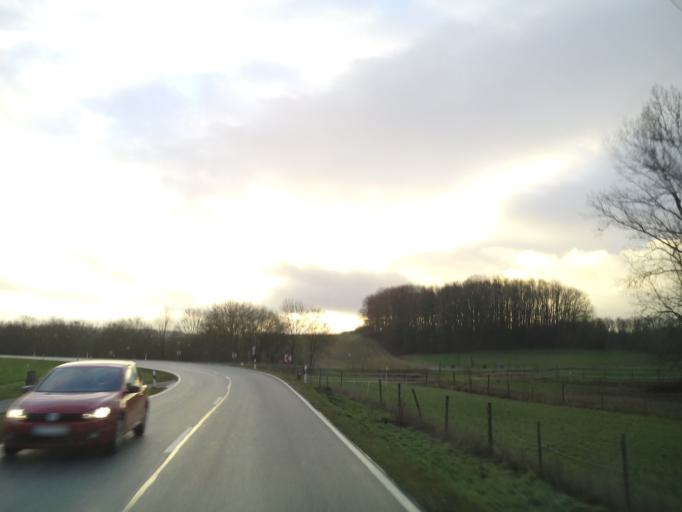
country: DE
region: Bavaria
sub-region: Upper Franconia
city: Untersiemau
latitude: 50.1859
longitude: 11.0012
